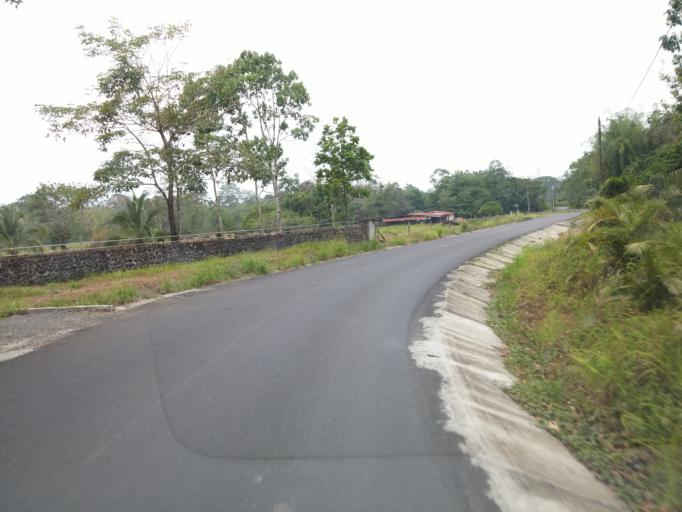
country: CR
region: Alajuela
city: Quesada
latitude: 10.3232
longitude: -84.5132
